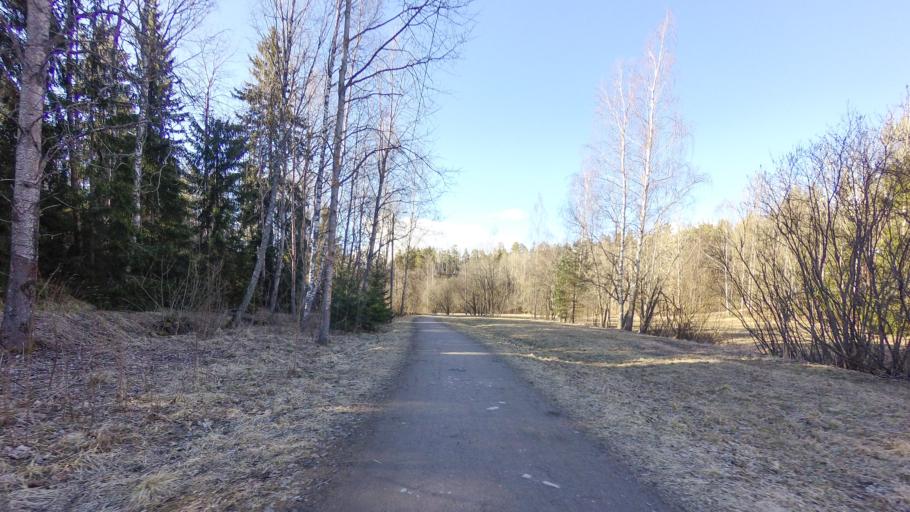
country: FI
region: Uusimaa
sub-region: Helsinki
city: Helsinki
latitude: 60.1725
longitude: 25.0280
